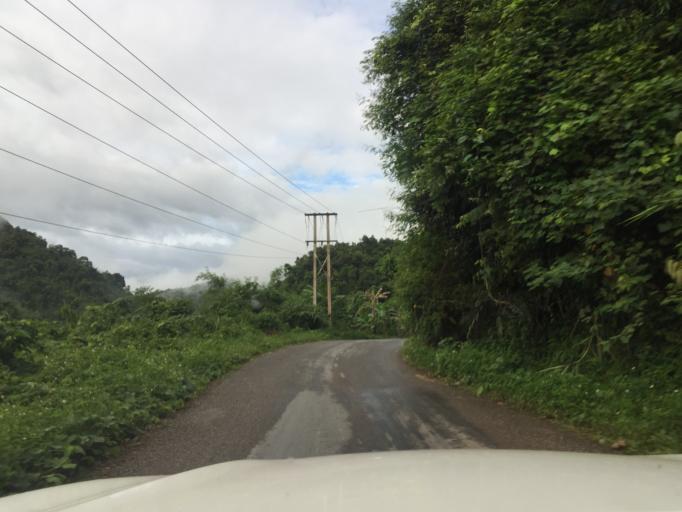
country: LA
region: Phongsali
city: Khoa
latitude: 21.0945
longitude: 102.2482
